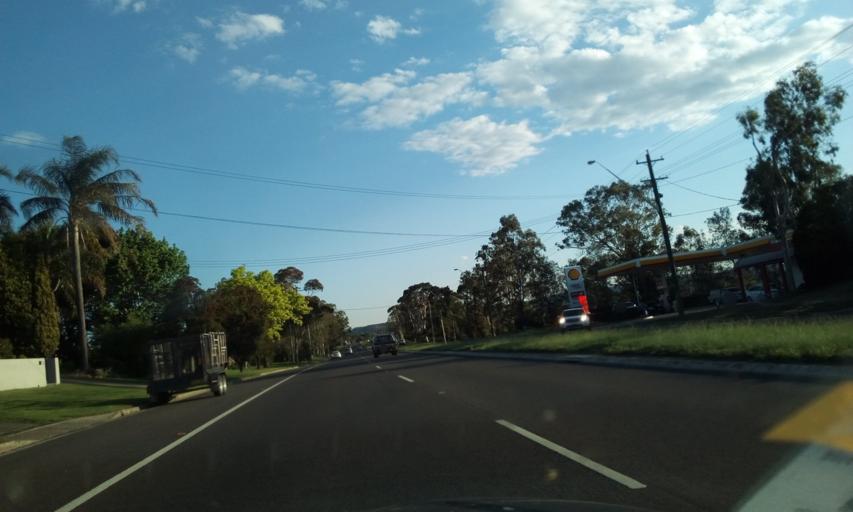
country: AU
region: New South Wales
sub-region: Camden
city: Camden South
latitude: -34.0857
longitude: 150.6952
